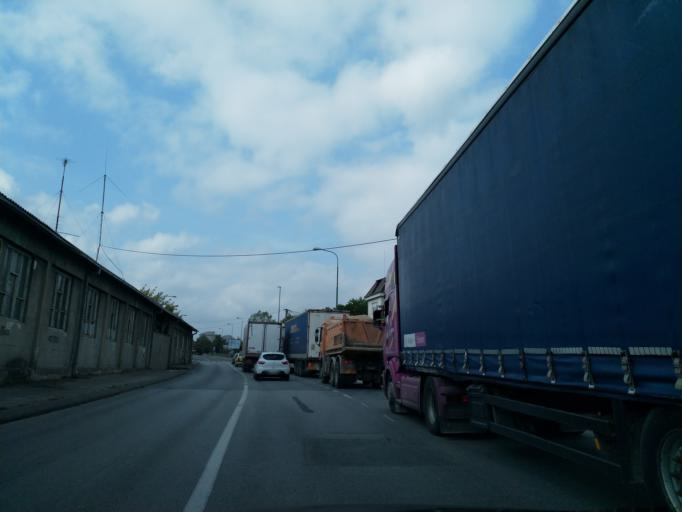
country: RS
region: Central Serbia
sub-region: Sumadijski Okrug
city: Kragujevac
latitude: 44.0289
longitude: 20.9178
